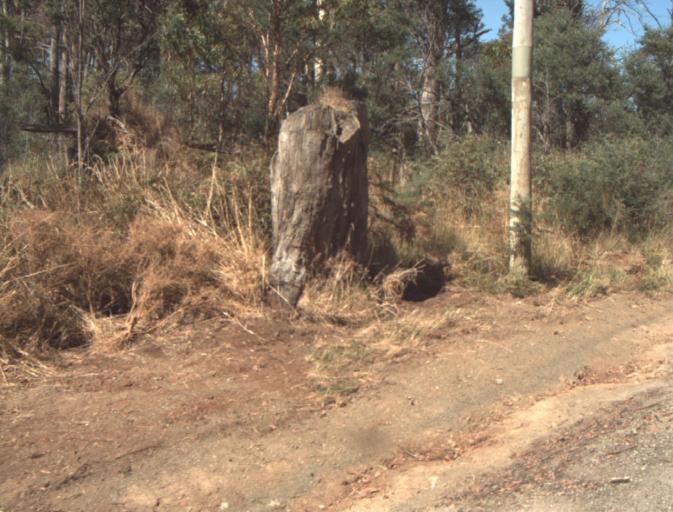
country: AU
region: Tasmania
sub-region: Launceston
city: Newstead
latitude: -41.3675
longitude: 147.2440
